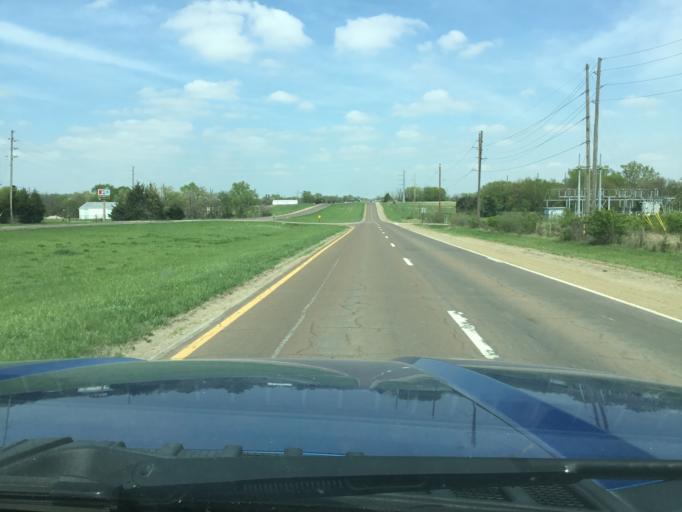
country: US
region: Kansas
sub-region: Osage County
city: Carbondale
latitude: 38.9217
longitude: -95.6875
